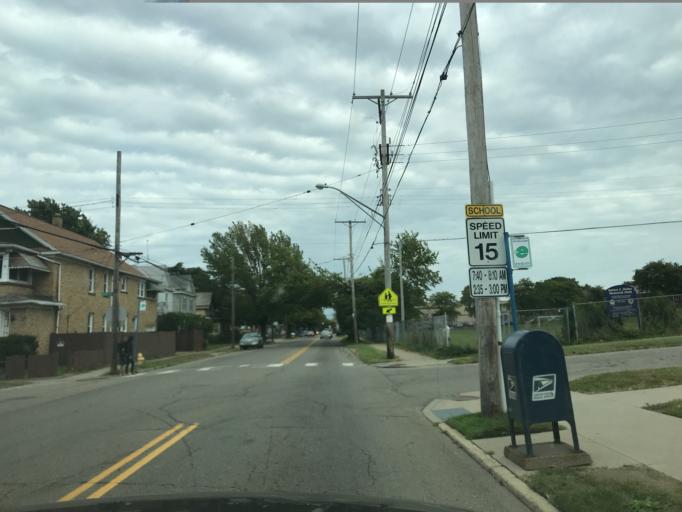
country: US
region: Pennsylvania
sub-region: Erie County
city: Erie
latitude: 42.1174
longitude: -80.0583
